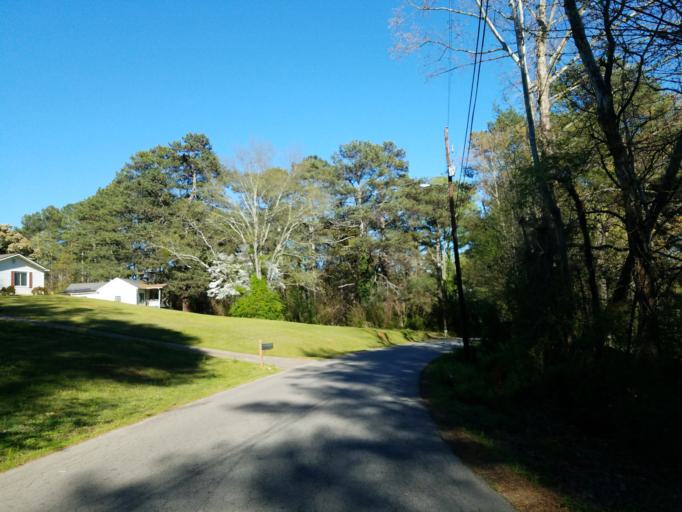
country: US
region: Georgia
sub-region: Cobb County
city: Marietta
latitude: 33.9621
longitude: -84.5067
